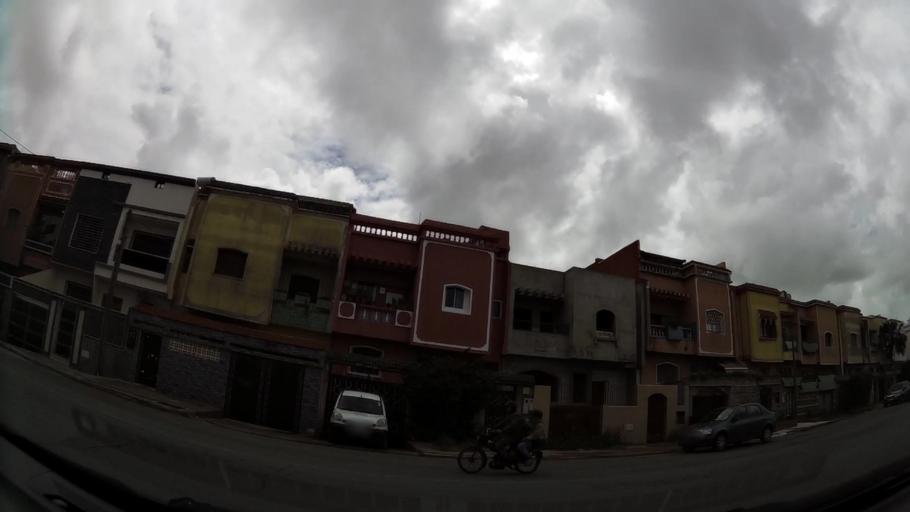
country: MA
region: Grand Casablanca
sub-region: Casablanca
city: Casablanca
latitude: 33.5319
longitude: -7.5962
